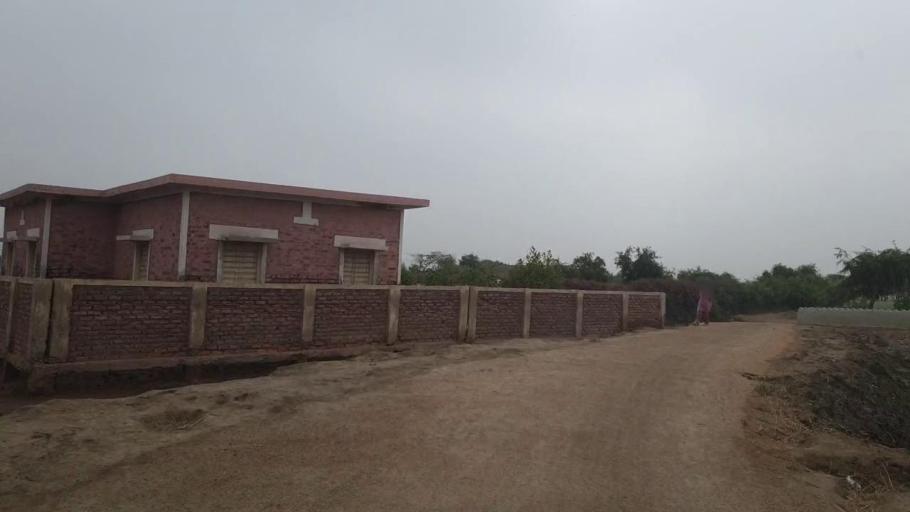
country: PK
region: Sindh
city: Badin
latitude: 24.5682
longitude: 68.6641
